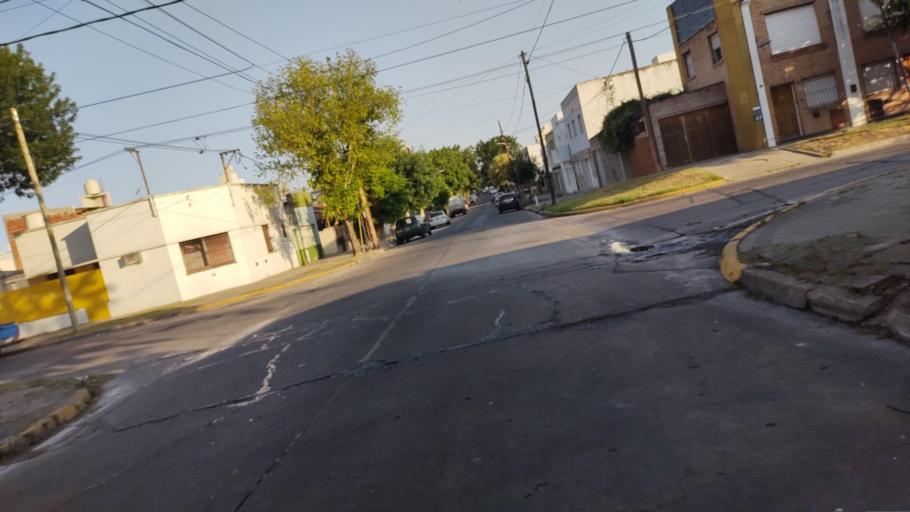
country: AR
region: Buenos Aires
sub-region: Partido de La Plata
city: La Plata
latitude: -34.9317
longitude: -57.9728
